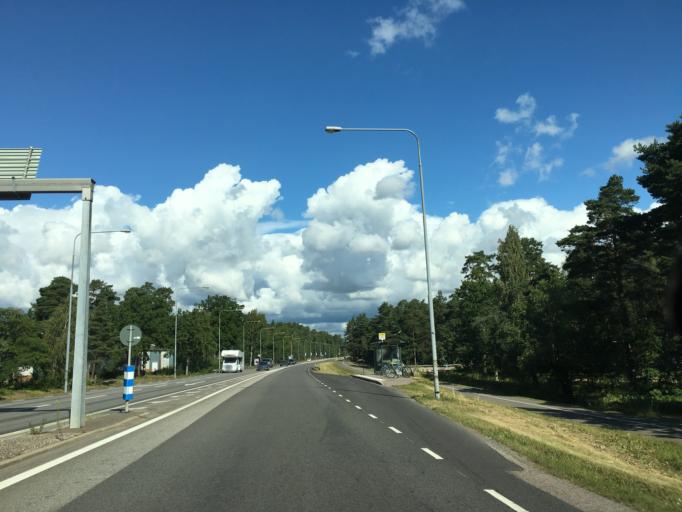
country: SE
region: Kalmar
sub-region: Kalmar Kommun
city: Kalmar
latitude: 56.6791
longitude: 16.3601
